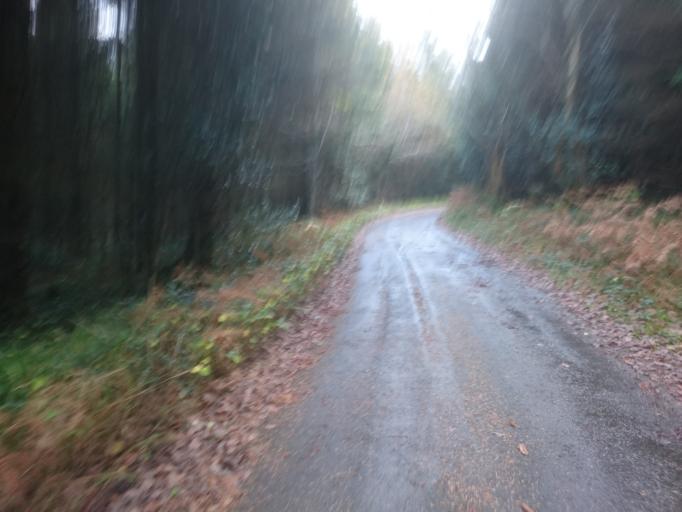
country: IE
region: Leinster
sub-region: Kilkenny
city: Thomastown
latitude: 52.4669
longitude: -7.0537
